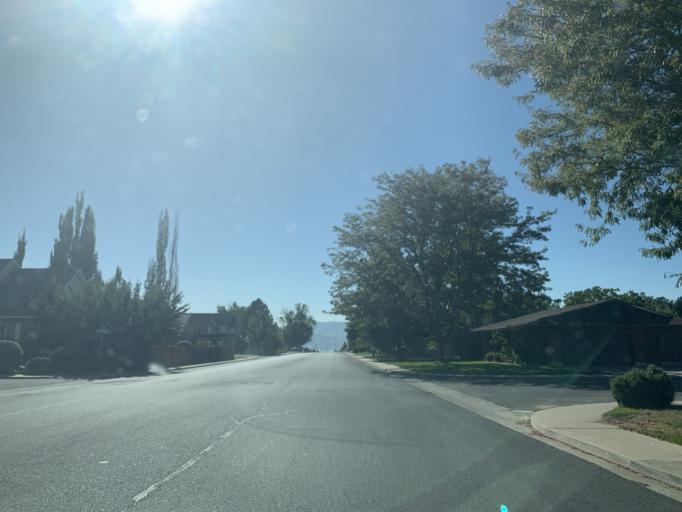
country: US
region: Utah
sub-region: Utah County
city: Orem
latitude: 40.2572
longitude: -111.6926
